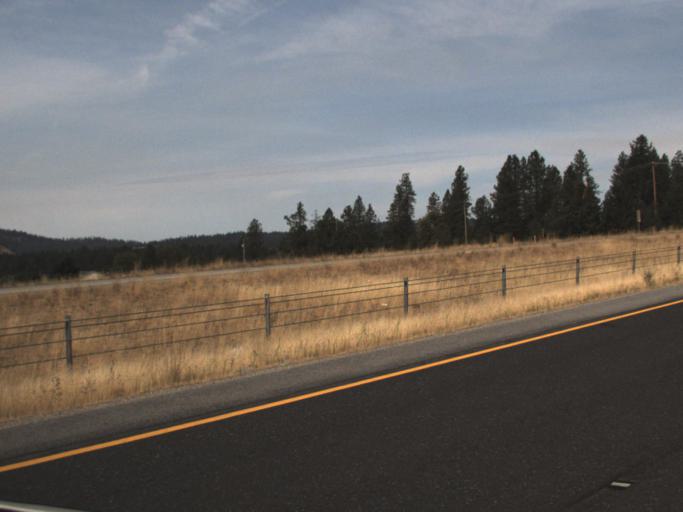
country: US
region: Washington
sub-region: Spokane County
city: Fairwood
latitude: 47.8296
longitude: -117.4179
